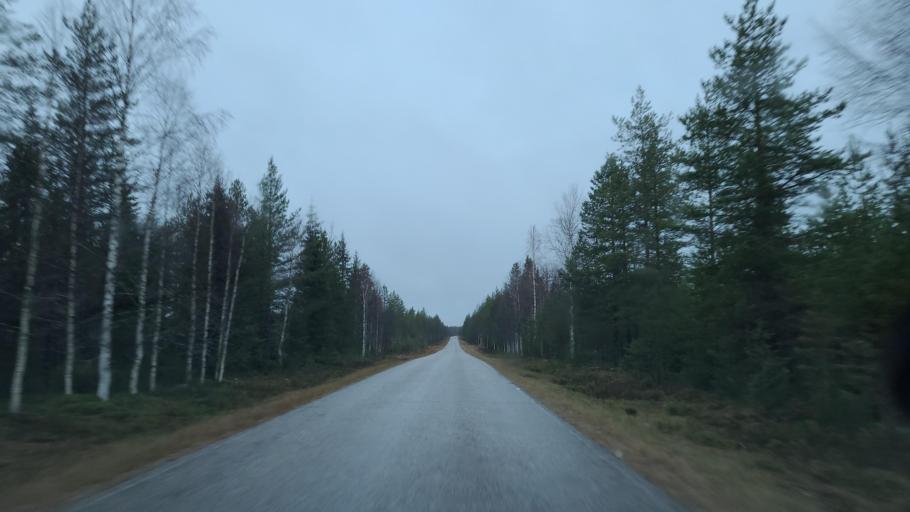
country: FI
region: Lapland
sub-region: Kemi-Tornio
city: Simo
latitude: 65.8921
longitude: 25.2151
